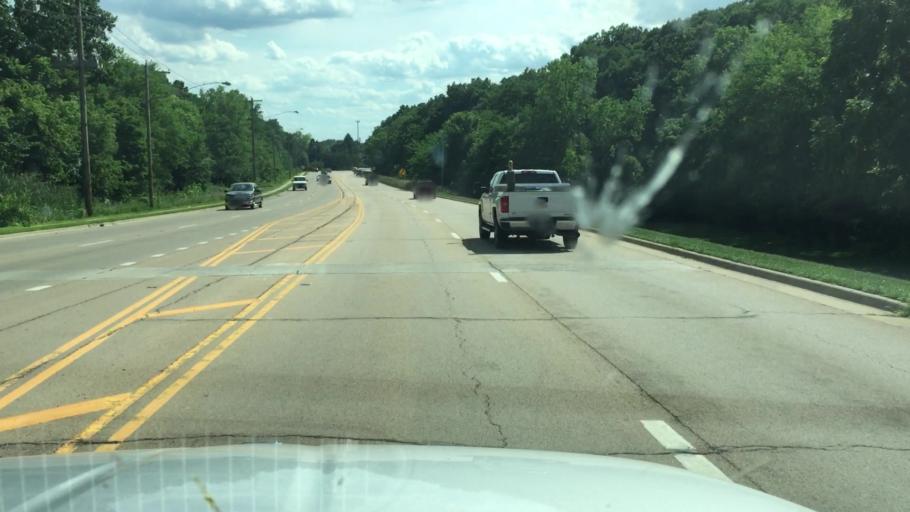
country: US
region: Illinois
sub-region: LaSalle County
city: Ottawa
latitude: 41.3662
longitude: -88.8371
